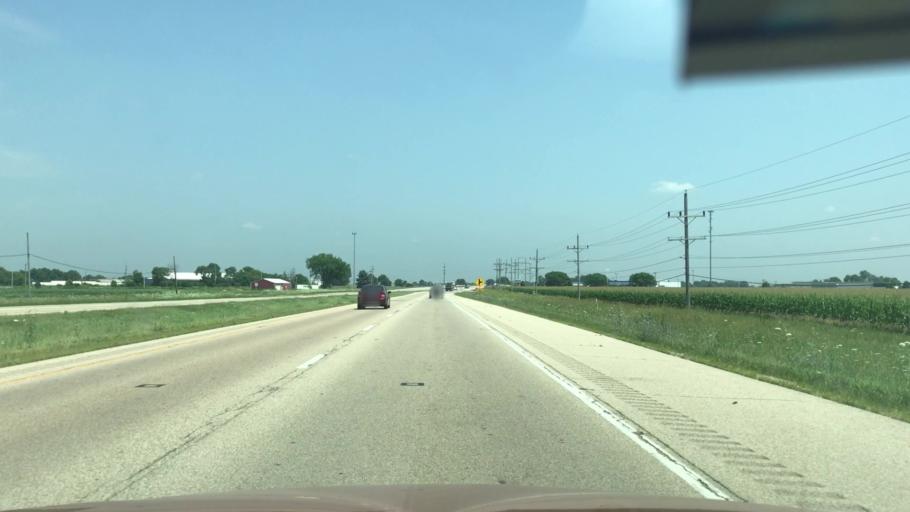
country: US
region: Illinois
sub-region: Winnebago County
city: Cherry Valley
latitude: 42.2388
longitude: -88.9249
